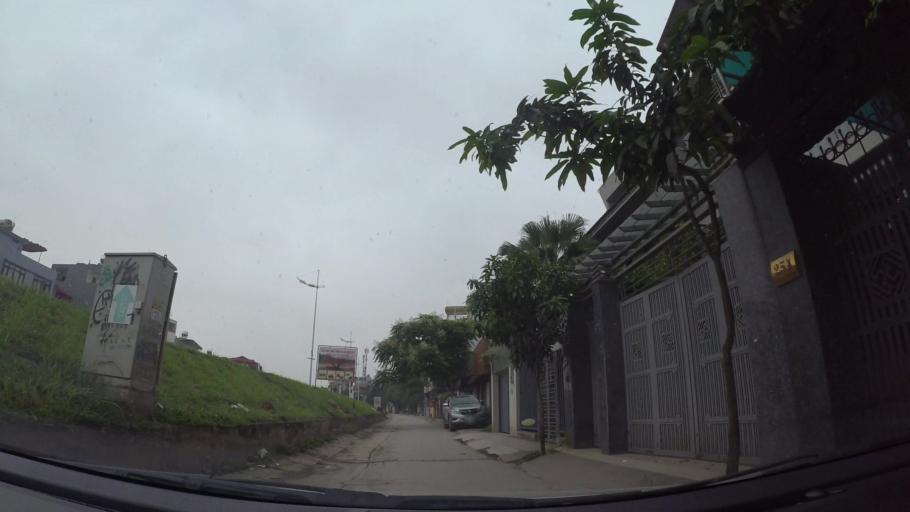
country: VN
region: Ha Noi
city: Tay Ho
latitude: 21.0723
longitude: 105.8275
